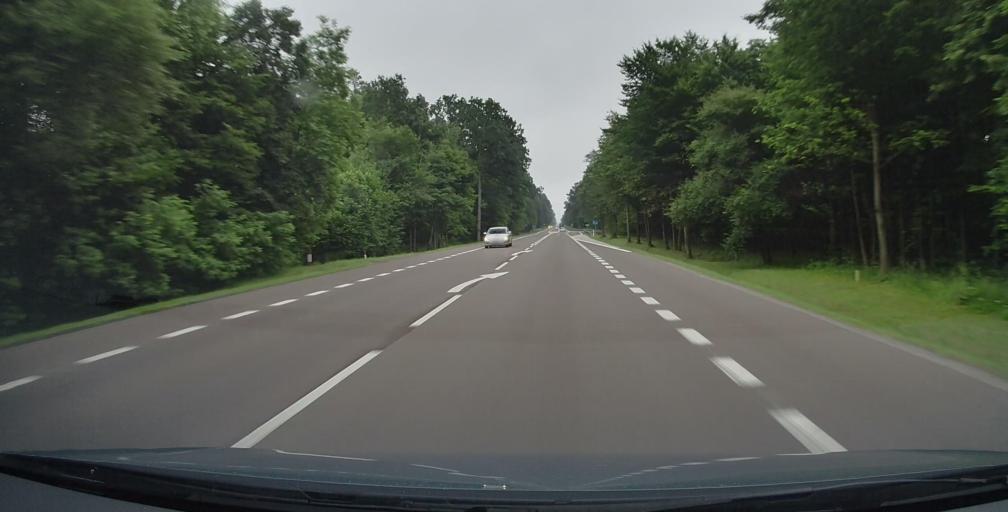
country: PL
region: Lublin Voivodeship
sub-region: Powiat bialski
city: Zalesie
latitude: 52.0362
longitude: 23.4221
